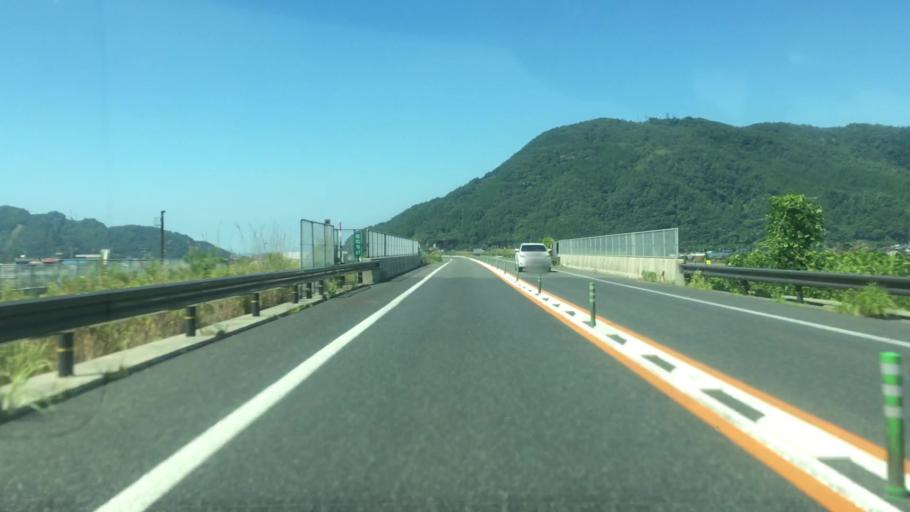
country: JP
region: Tottori
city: Tottori
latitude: 35.3941
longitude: 134.2039
